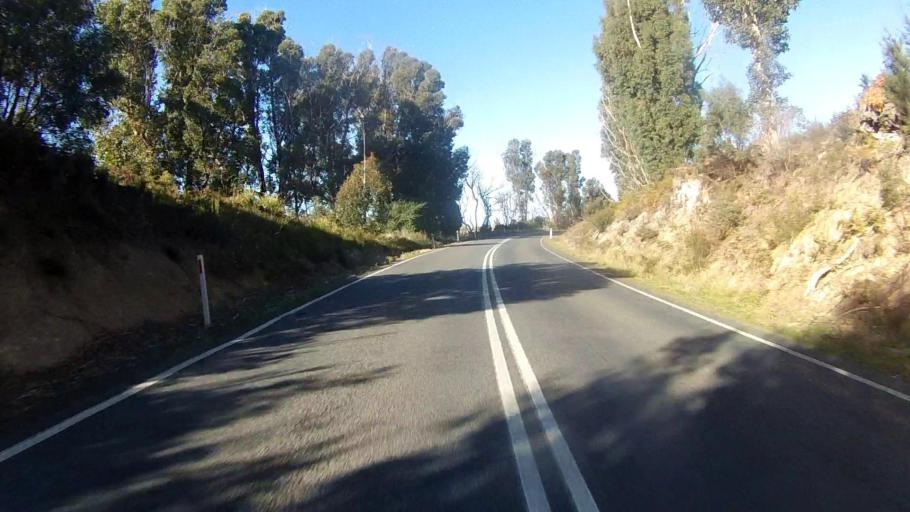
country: AU
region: Tasmania
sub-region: Sorell
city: Sorell
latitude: -42.8394
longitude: 147.8084
